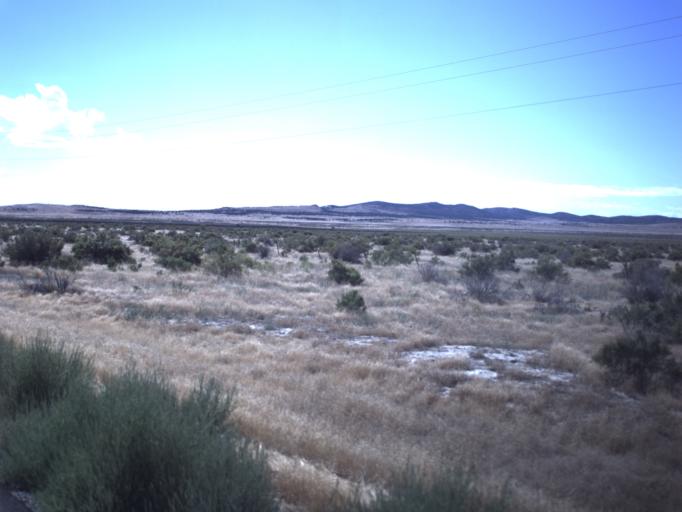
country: US
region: Utah
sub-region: Tooele County
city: Grantsville
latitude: 40.2632
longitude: -112.6894
